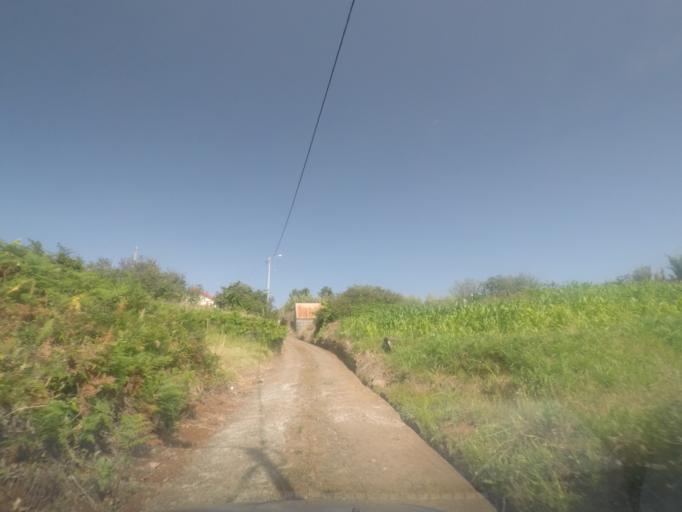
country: PT
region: Madeira
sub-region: Calheta
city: Faja da Ovelha
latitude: 32.8076
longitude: -17.2483
